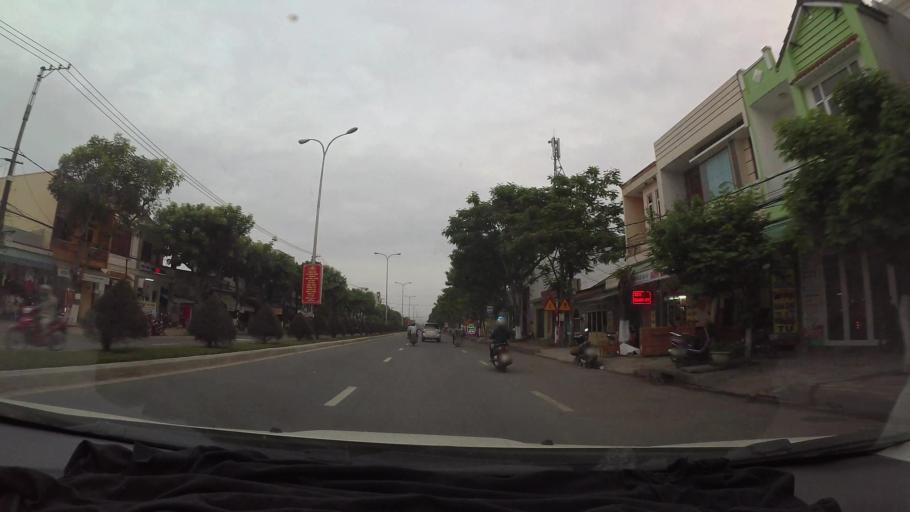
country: VN
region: Da Nang
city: Lien Chieu
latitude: 16.1053
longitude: 108.1328
